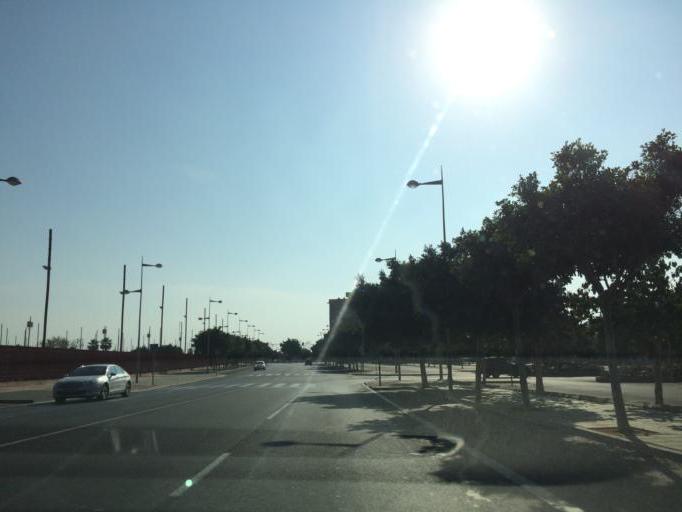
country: ES
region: Andalusia
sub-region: Provincia de Almeria
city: Almeria
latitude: 36.8398
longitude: -2.4323
